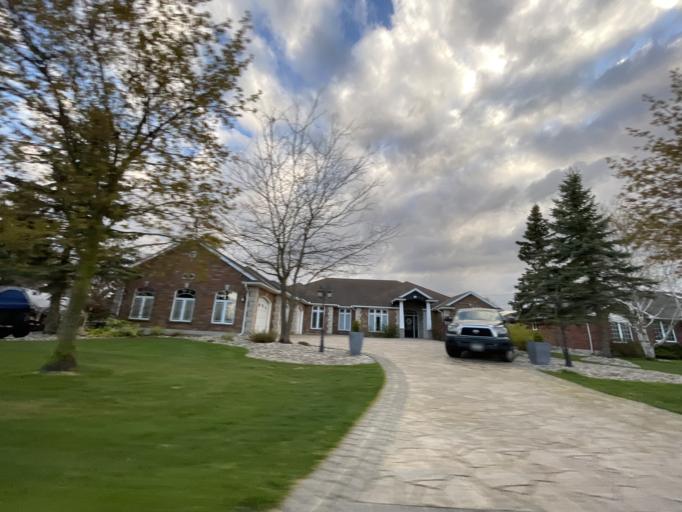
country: CA
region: Ontario
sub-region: Wellington County
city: Guelph
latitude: 43.5835
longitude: -80.2813
